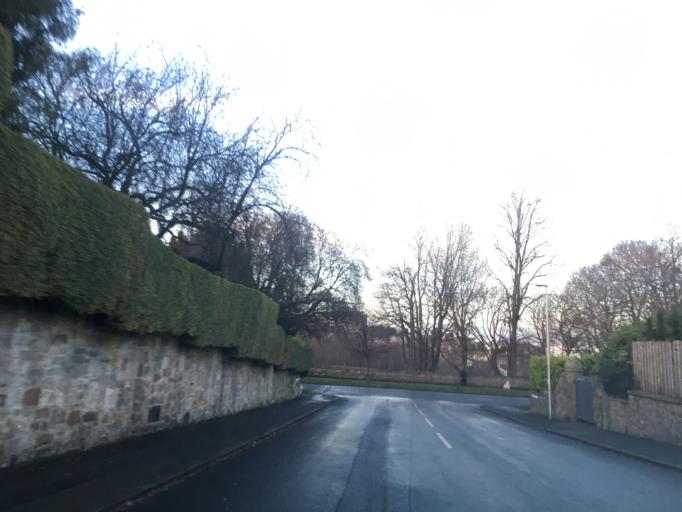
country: GB
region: Scotland
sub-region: Edinburgh
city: Colinton
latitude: 55.9501
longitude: -3.2480
